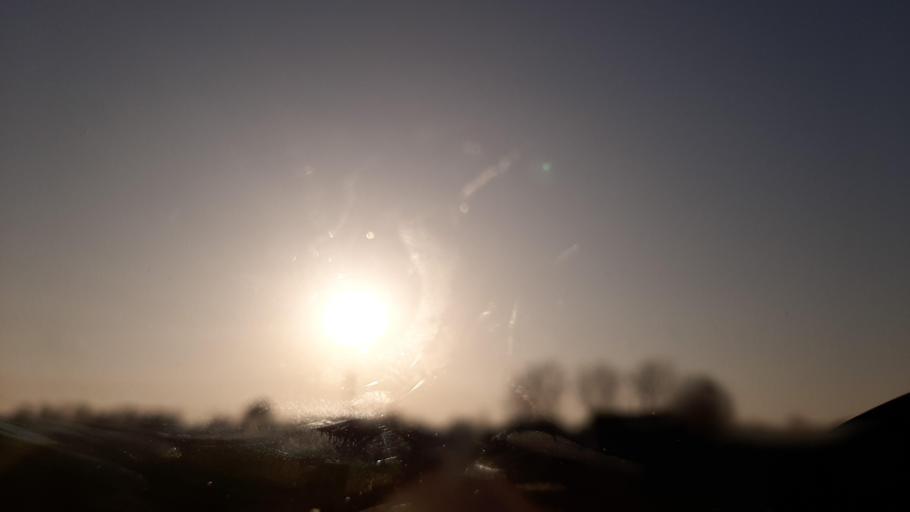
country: PL
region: Lublin Voivodeship
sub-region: Powiat lubelski
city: Garbow
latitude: 51.3927
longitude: 22.3821
